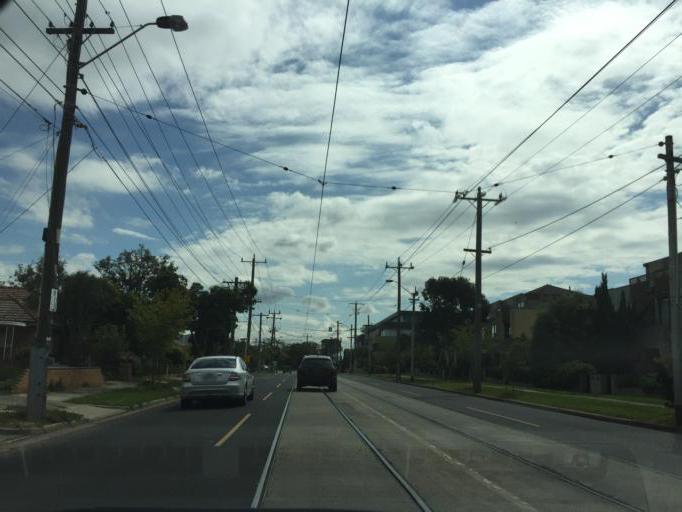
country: AU
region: Victoria
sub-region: Maribyrnong
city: Maribyrnong
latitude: -37.7825
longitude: 144.8912
